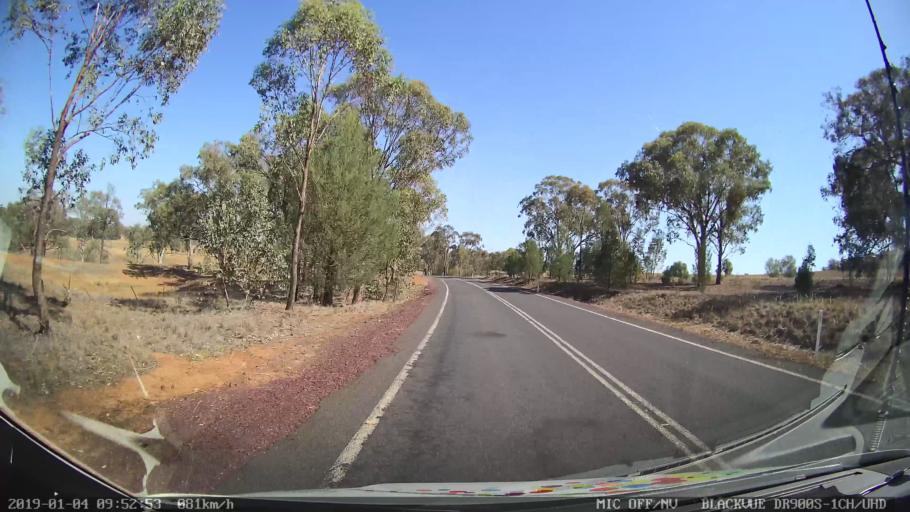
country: AU
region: New South Wales
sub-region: Cabonne
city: Canowindra
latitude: -33.5585
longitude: 148.4243
